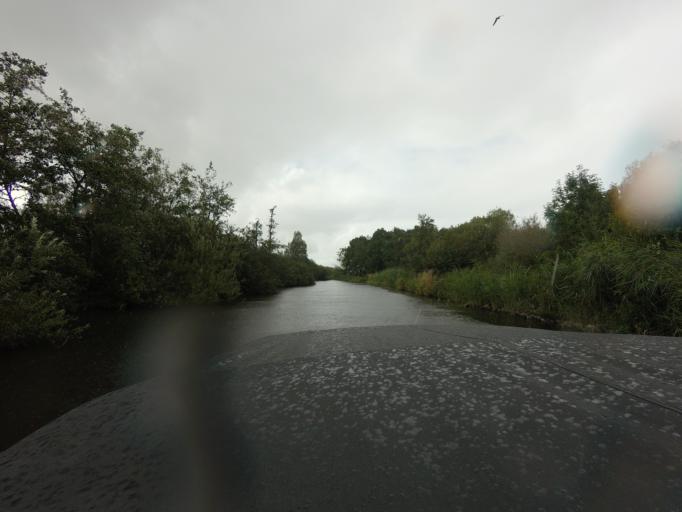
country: NL
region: Friesland
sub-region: Gemeente Boarnsterhim
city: Warten
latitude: 53.1369
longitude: 5.9087
